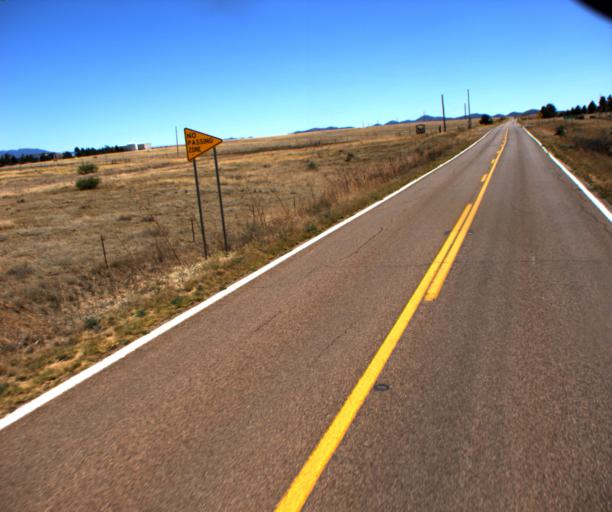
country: US
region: Arizona
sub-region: Cochise County
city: Huachuca City
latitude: 31.6607
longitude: -110.6049
